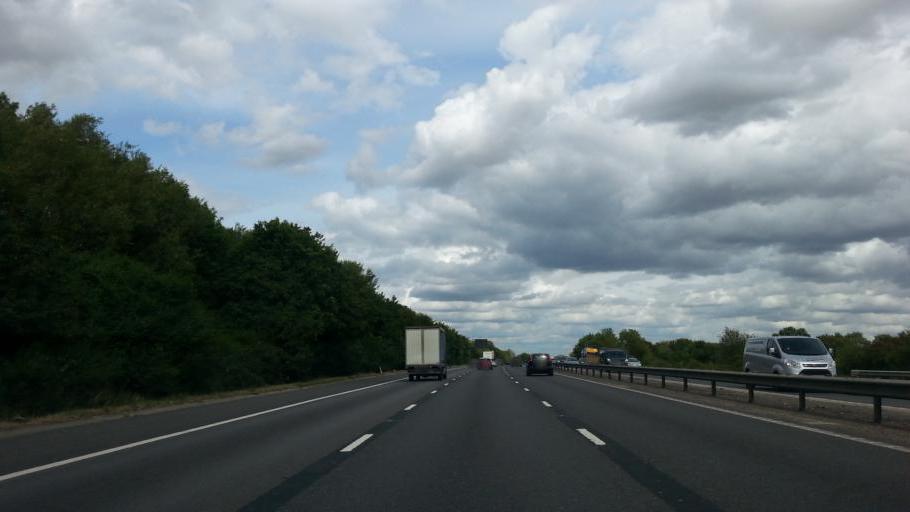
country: GB
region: England
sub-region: Essex
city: Harlow
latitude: 51.7625
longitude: 0.1502
